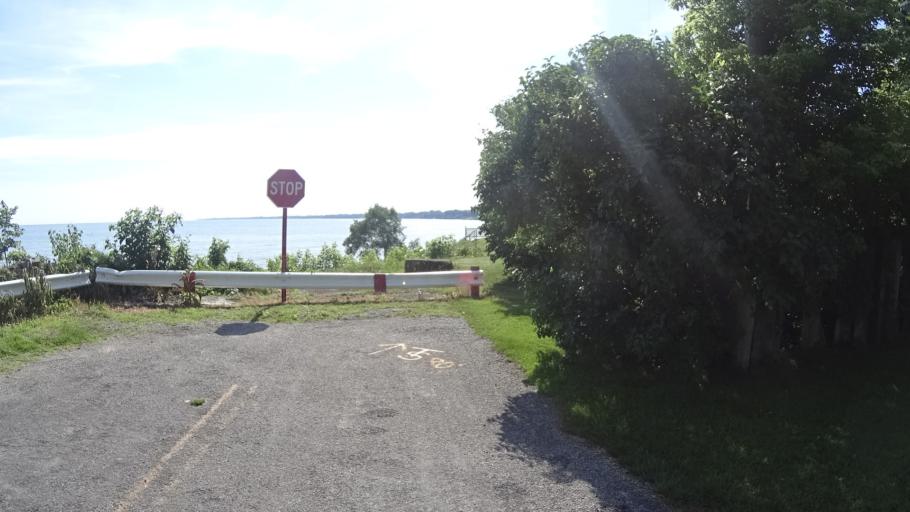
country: US
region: Ohio
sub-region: Erie County
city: Huron
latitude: 41.3824
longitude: -82.5061
